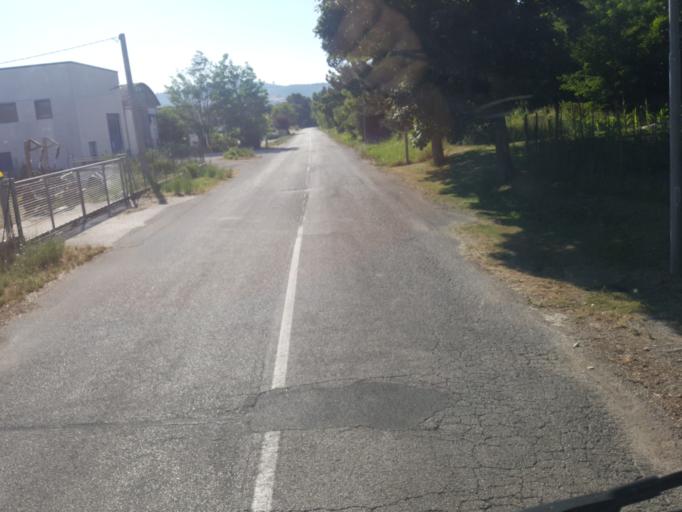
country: IT
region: The Marches
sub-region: Provincia di Pesaro e Urbino
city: Montecalvo in Foglia
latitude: 43.7845
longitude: 12.6304
